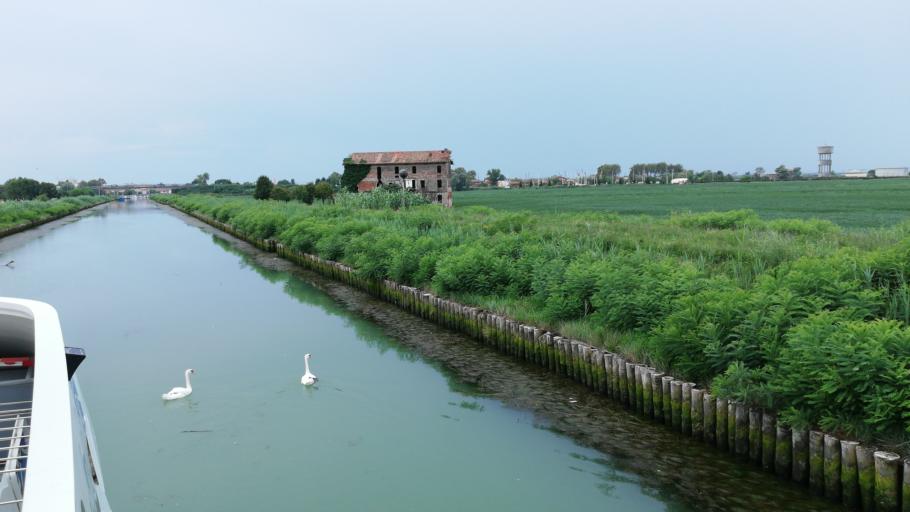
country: IT
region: Veneto
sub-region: Provincia di Venezia
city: Caorle
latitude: 45.6115
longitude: 12.8809
